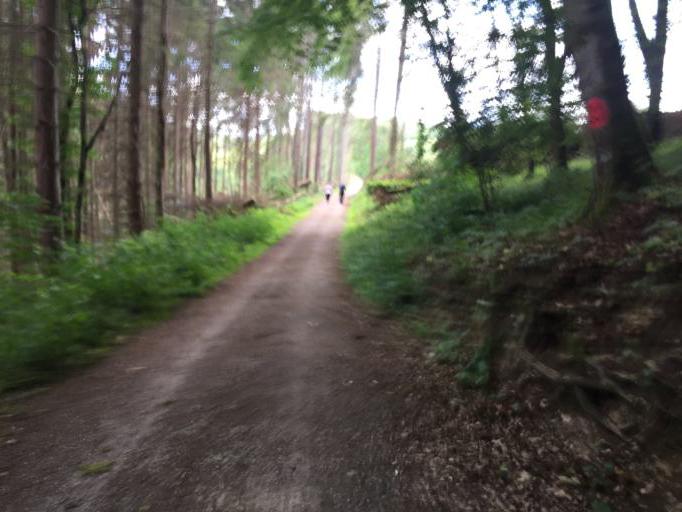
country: DE
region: Rheinland-Pfalz
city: Heiligenroth
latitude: 50.4255
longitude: 7.8582
